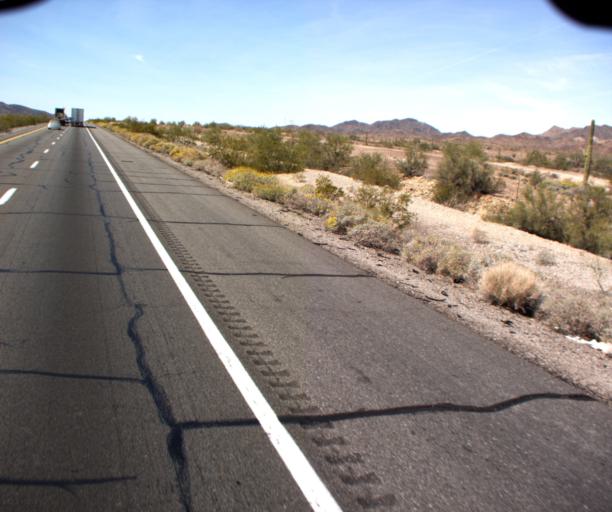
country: US
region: Arizona
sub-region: La Paz County
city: Quartzsite
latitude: 33.6509
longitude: -114.3040
